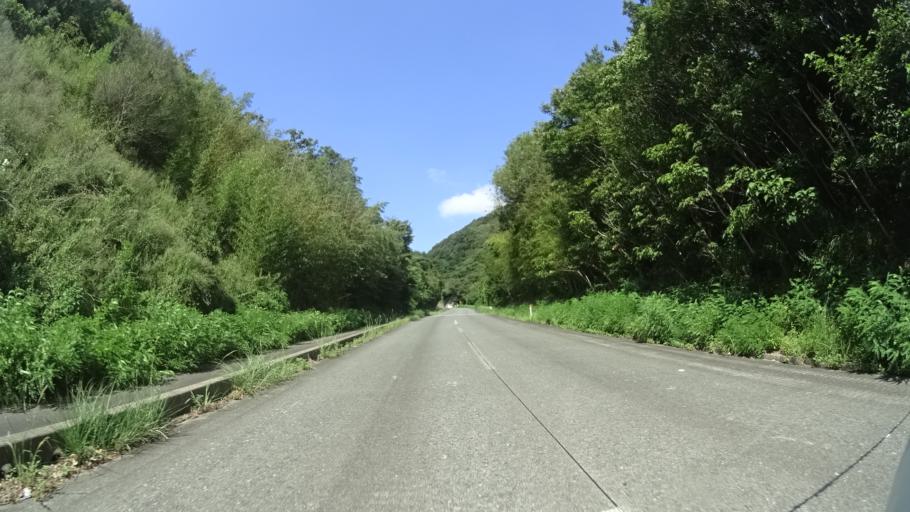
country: JP
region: Yamaguchi
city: Shimonoseki
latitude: 34.0959
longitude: 130.8924
